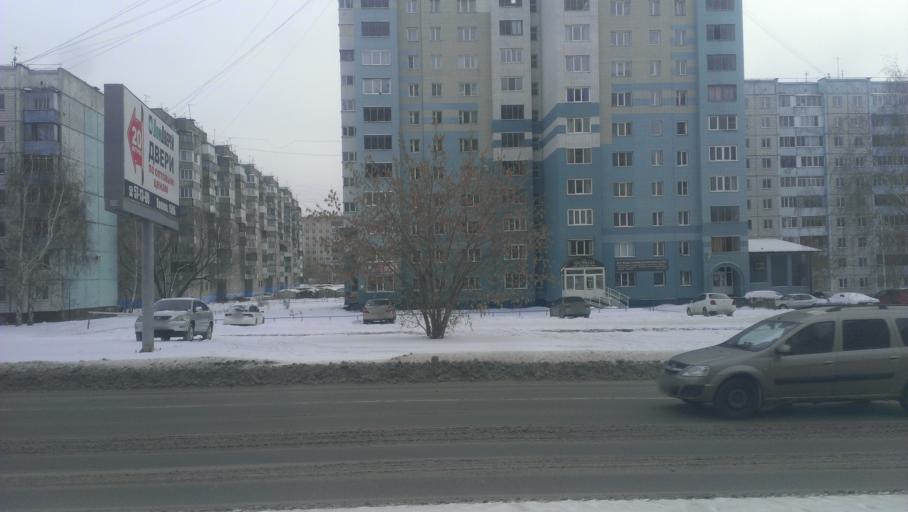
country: RU
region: Altai Krai
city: Novosilikatnyy
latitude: 53.3491
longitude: 83.6725
